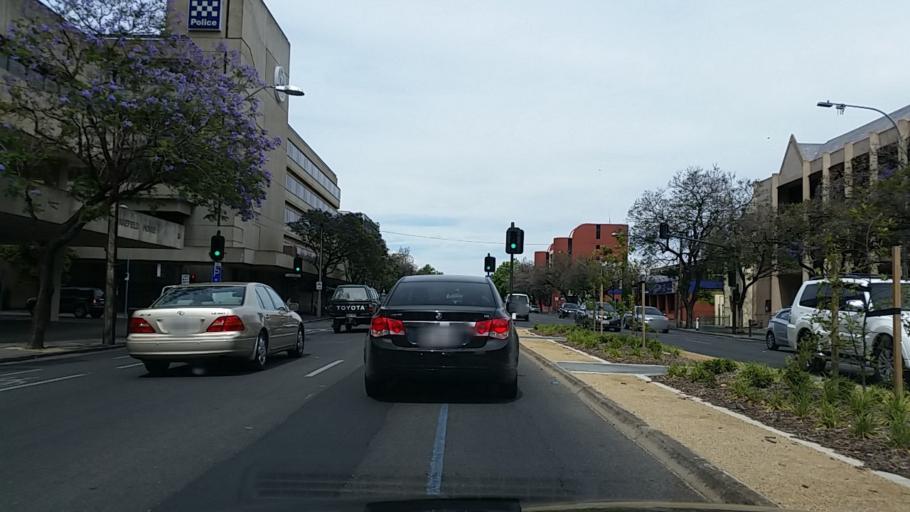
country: AU
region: South Australia
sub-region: Adelaide
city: Adelaide
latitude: -34.9285
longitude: 138.6017
